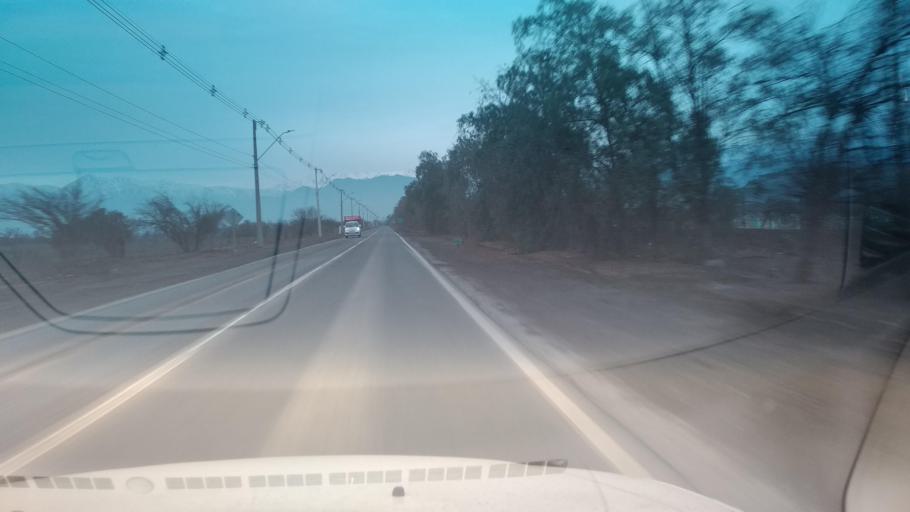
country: CL
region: Santiago Metropolitan
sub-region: Provincia de Chacabuco
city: Chicureo Abajo
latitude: -33.0944
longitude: -70.7464
